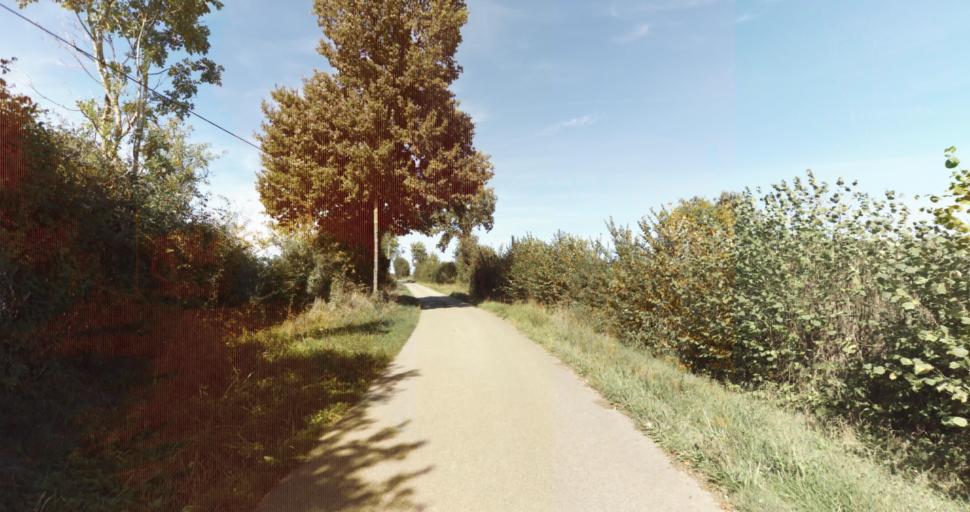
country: FR
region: Lower Normandy
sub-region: Departement de l'Orne
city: Gace
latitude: 48.7586
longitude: 0.2433
